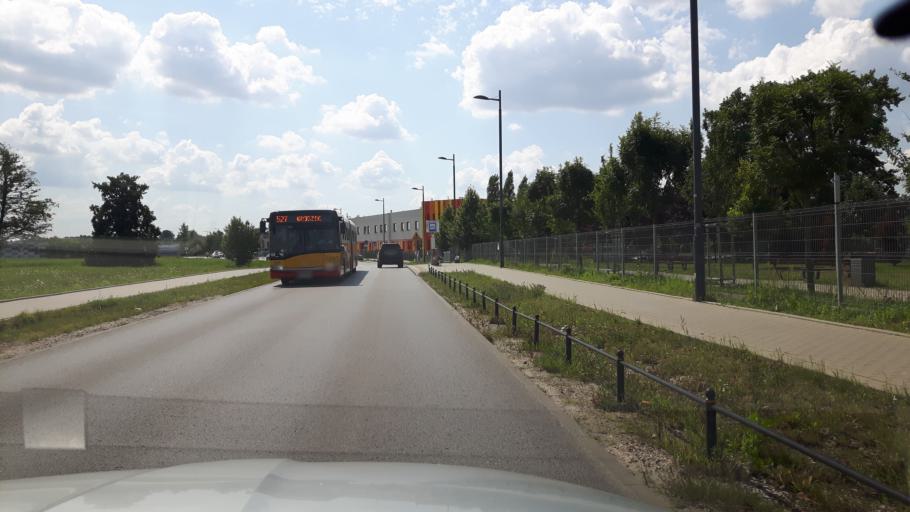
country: PL
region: Masovian Voivodeship
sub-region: Warszawa
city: Targowek
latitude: 52.3127
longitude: 21.0607
